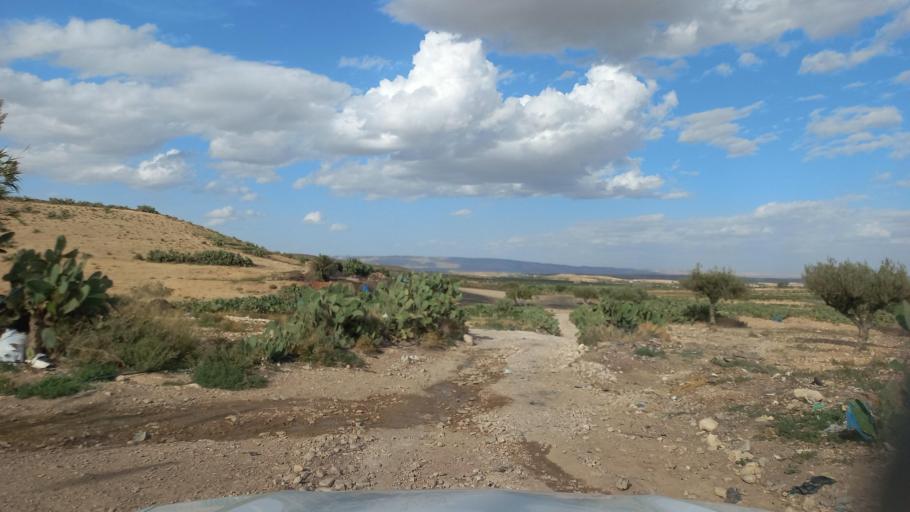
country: TN
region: Al Qasrayn
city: Sbiba
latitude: 35.4510
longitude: 9.0887
